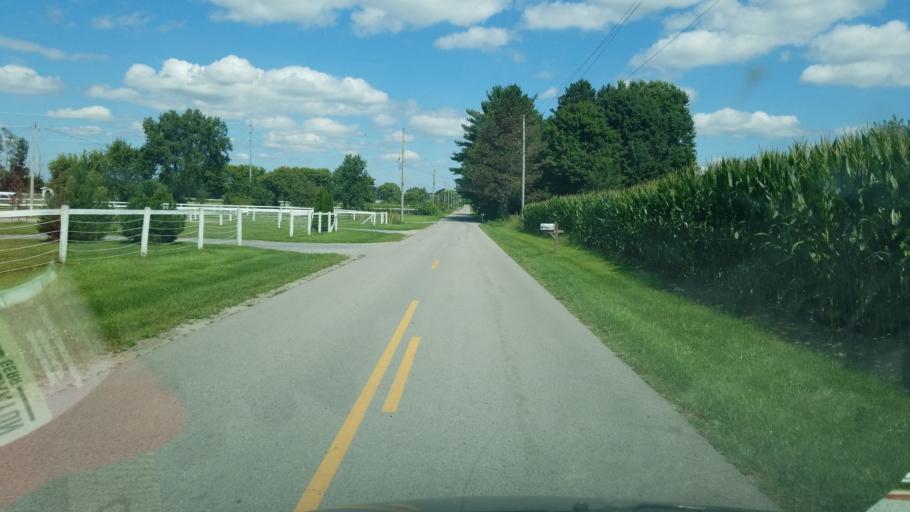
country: US
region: Ohio
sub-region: Henry County
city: Liberty Center
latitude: 41.4662
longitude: -83.9413
